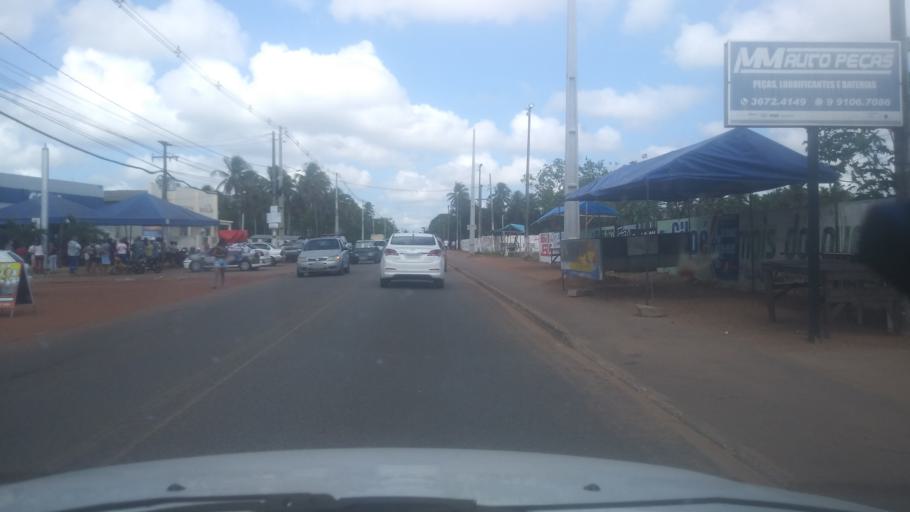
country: BR
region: Rio Grande do Norte
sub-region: Extremoz
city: Extremoz
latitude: -5.7051
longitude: -35.2958
